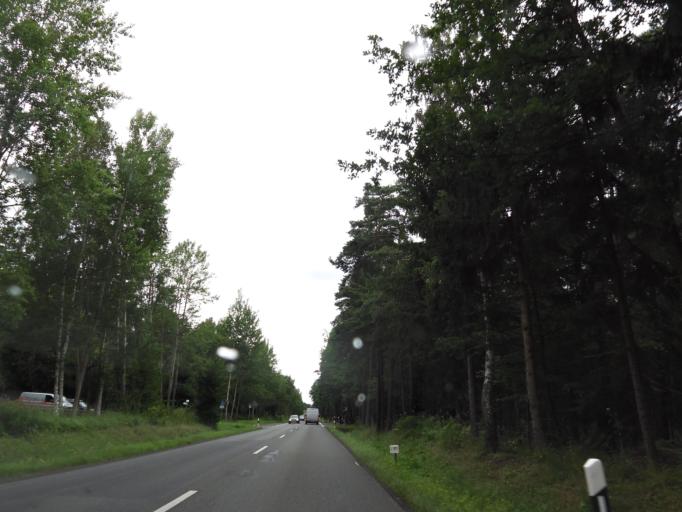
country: DE
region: Thuringia
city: Hermsdorf
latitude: 50.8760
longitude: 11.8512
